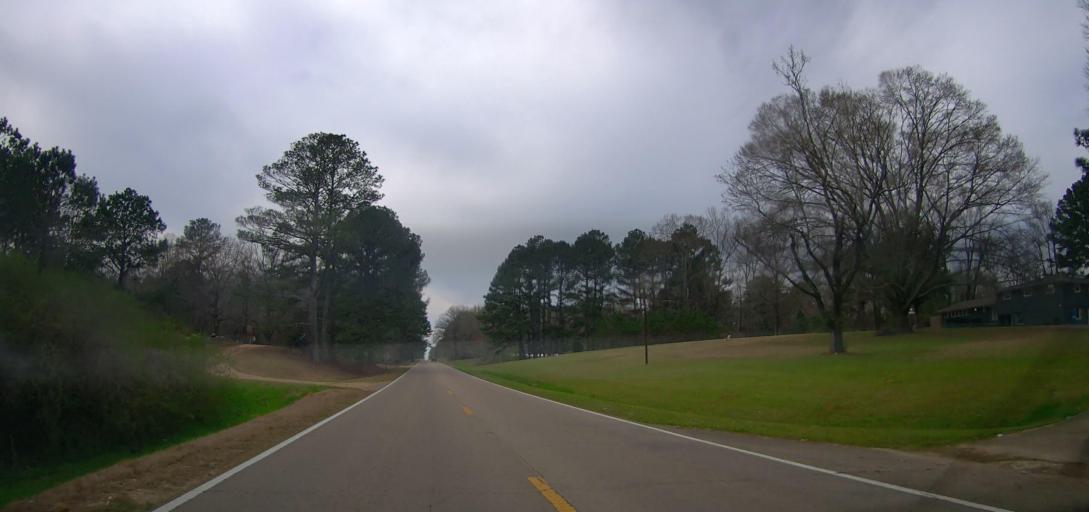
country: US
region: Mississippi
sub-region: Itawamba County
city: Mantachie
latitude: 34.2557
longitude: -88.4943
